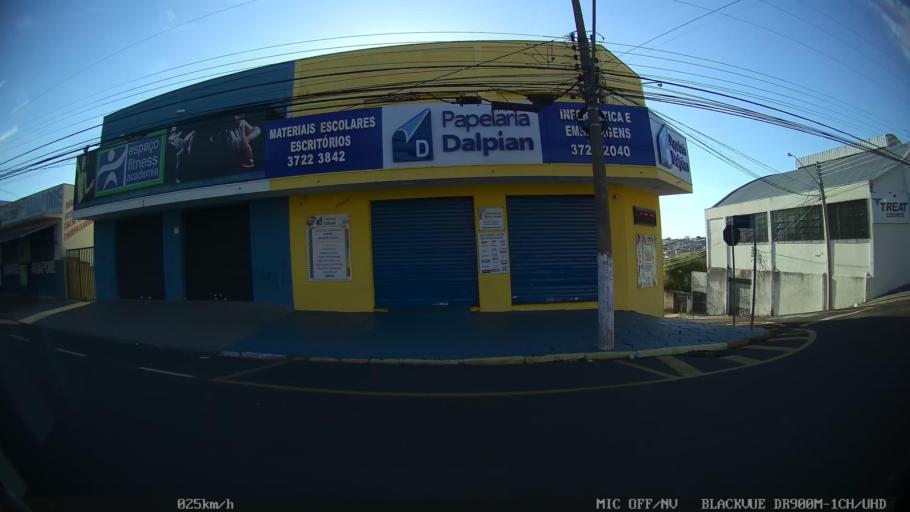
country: BR
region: Sao Paulo
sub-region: Franca
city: Franca
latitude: -20.5235
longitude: -47.3876
